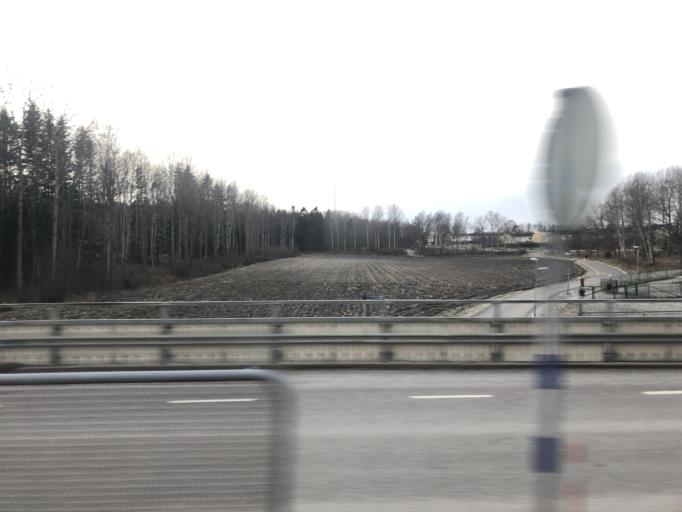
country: SE
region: Stockholm
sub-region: Jarfalla Kommun
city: Jakobsberg
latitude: 59.4130
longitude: 17.7970
